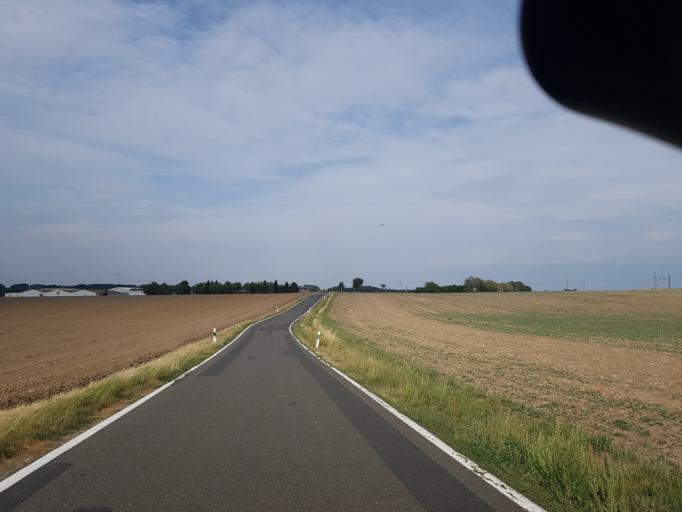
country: DE
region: Saxony
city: Stauchitz
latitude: 51.2305
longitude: 13.1923
